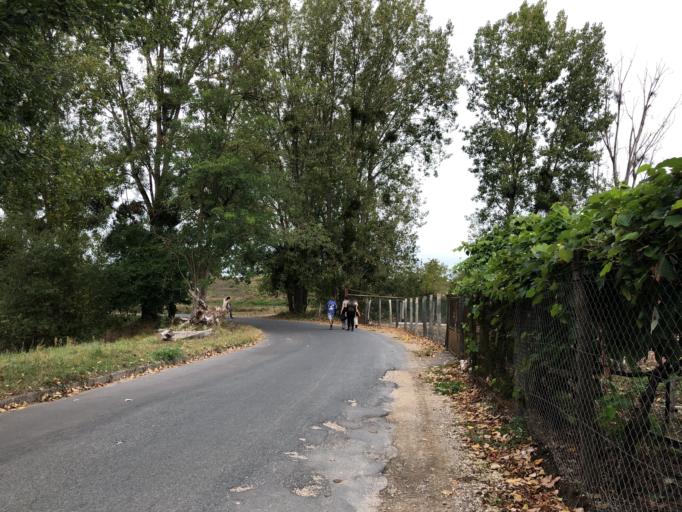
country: FR
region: Centre
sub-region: Departement du Loir-et-Cher
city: Saint-Gervais-la-Foret
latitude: 47.5685
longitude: 1.3415
